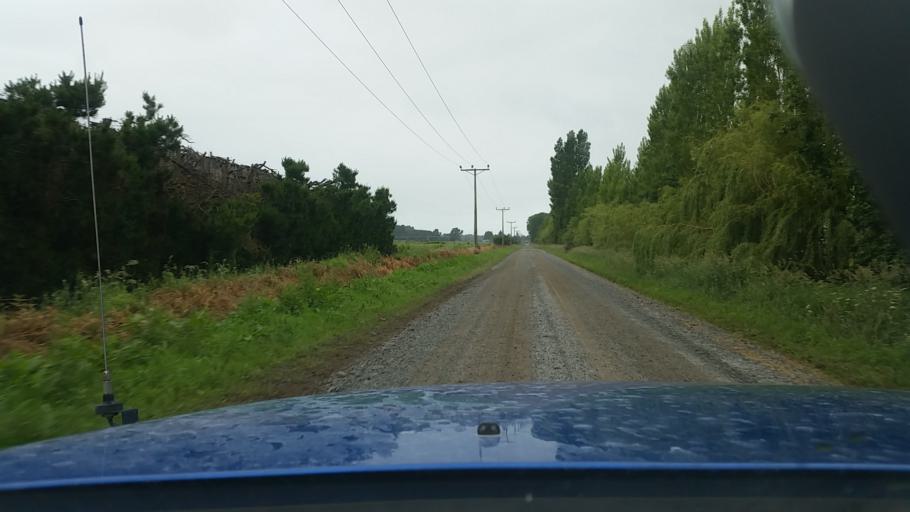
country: NZ
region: Canterbury
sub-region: Ashburton District
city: Tinwald
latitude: -44.0024
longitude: 171.6689
